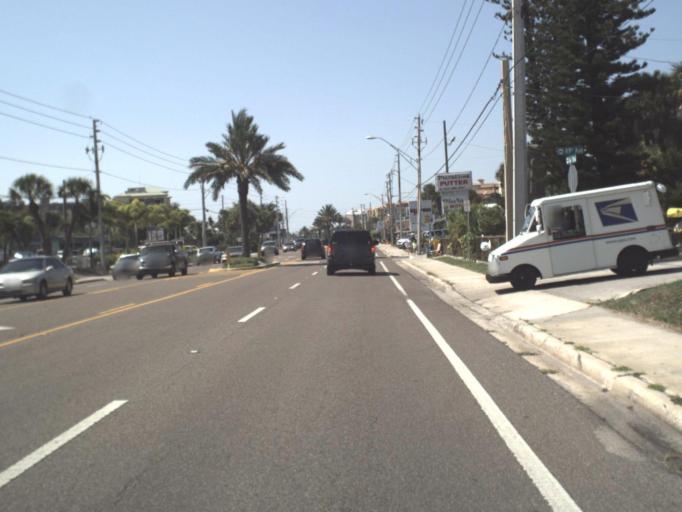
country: US
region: Florida
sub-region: Pinellas County
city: Saint Pete Beach
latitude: 27.7237
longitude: -82.7408
